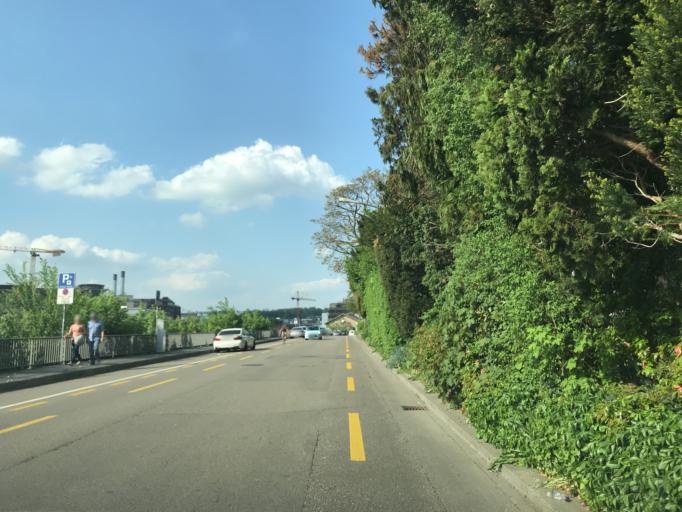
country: CH
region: Zurich
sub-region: Bezirk Winterthur
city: Stadt Winterthur (Kreis 1)
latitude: 47.4954
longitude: 8.7210
